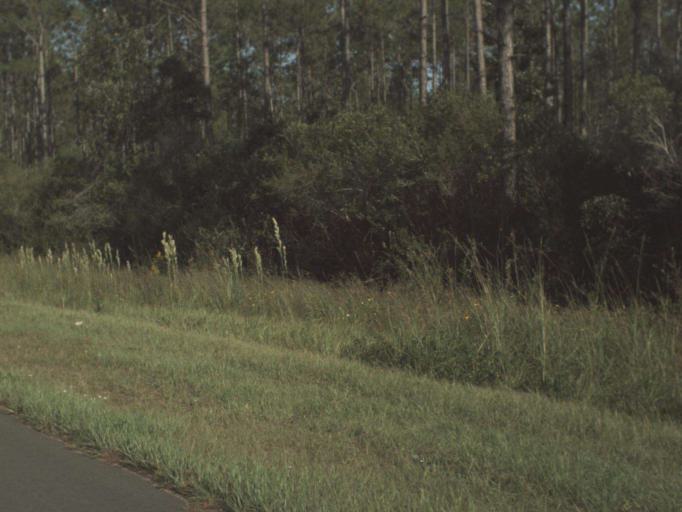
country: US
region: Florida
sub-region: Gulf County
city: Port Saint Joe
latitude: 29.8646
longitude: -85.2400
